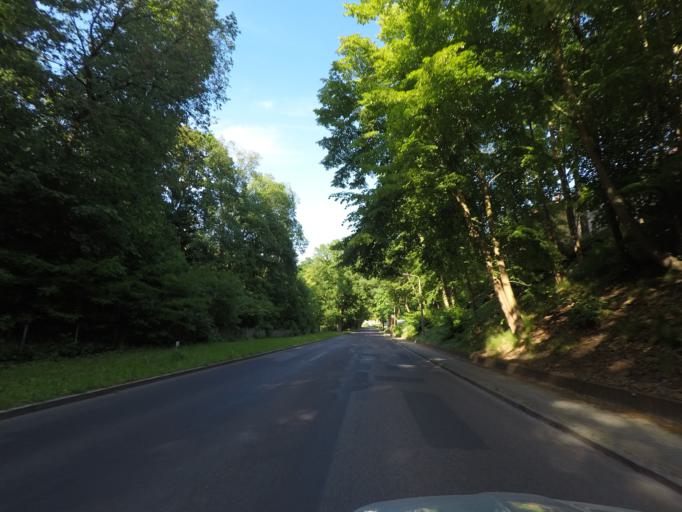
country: DE
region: Brandenburg
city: Bad Freienwalde
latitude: 52.7779
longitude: 14.0167
